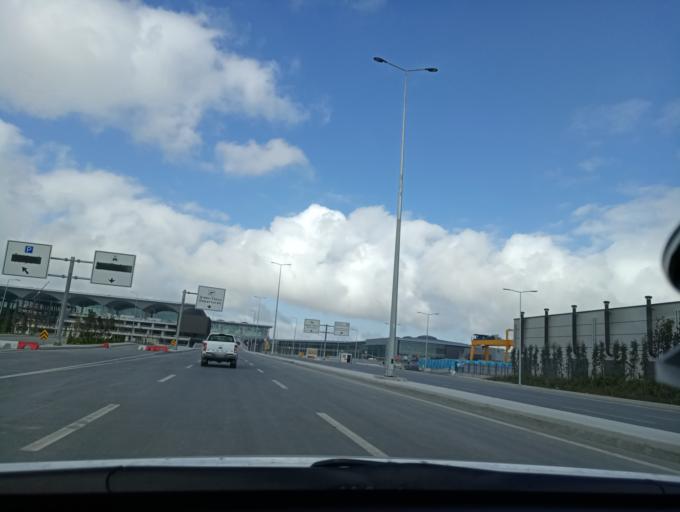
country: TR
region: Istanbul
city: Durusu
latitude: 41.2541
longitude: 28.7465
